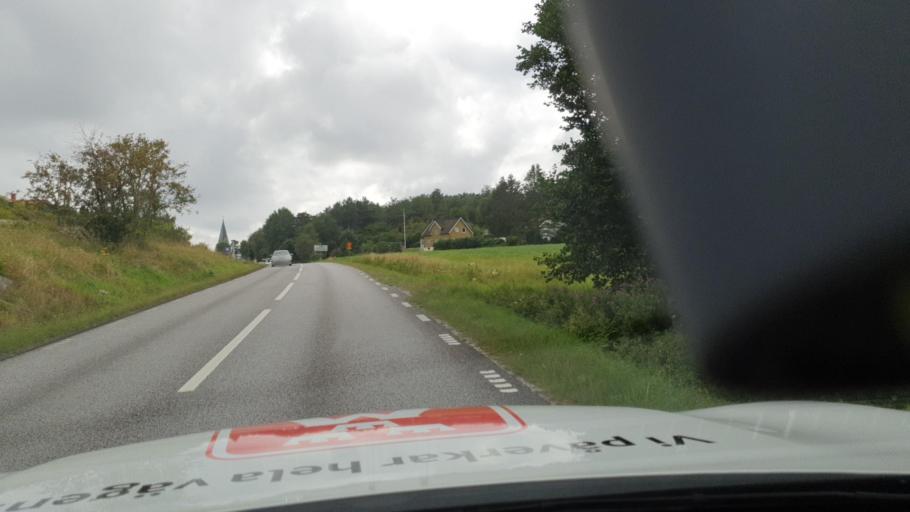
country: SE
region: Vaestra Goetaland
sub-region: Tanums Kommun
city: Grebbestad
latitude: 58.7014
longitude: 11.2565
